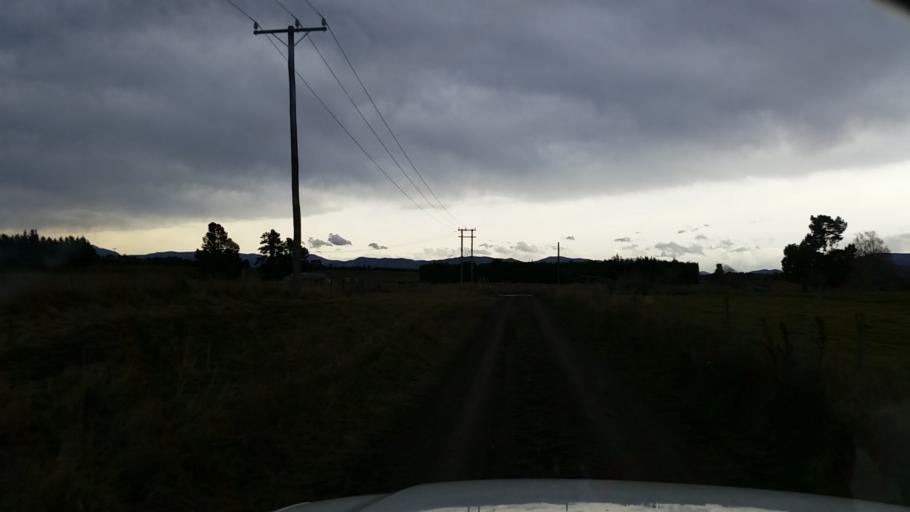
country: NZ
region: Canterbury
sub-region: Ashburton District
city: Methven
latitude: -43.6981
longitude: 171.4790
